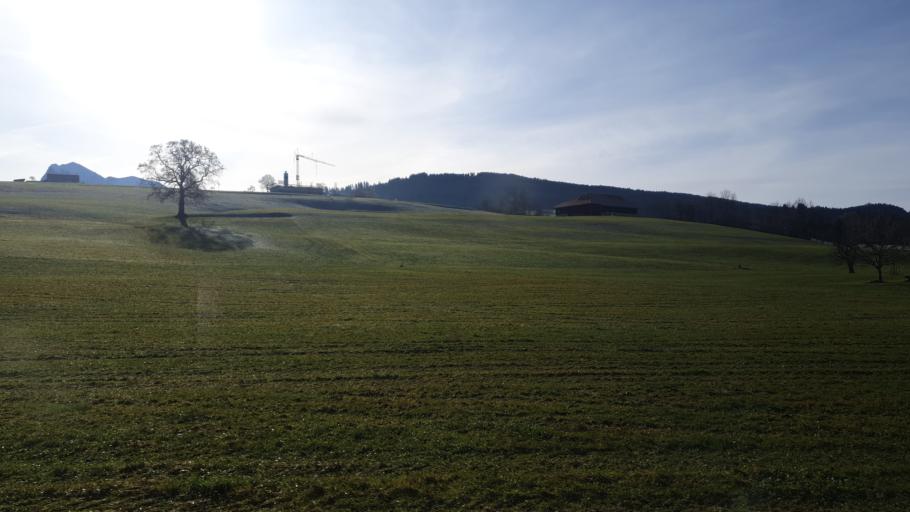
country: CH
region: Fribourg
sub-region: Gruyere District
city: Vuadens
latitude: 46.6168
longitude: 7.0016
